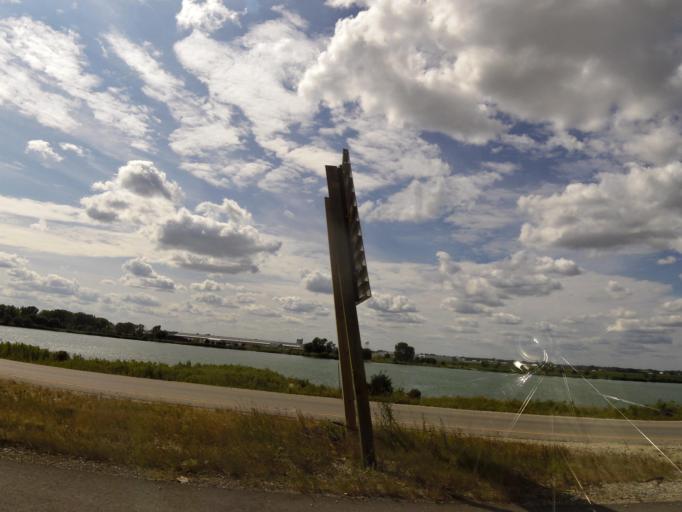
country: US
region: Illinois
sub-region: Ogle County
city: Rochelle
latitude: 41.9094
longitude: -89.0231
